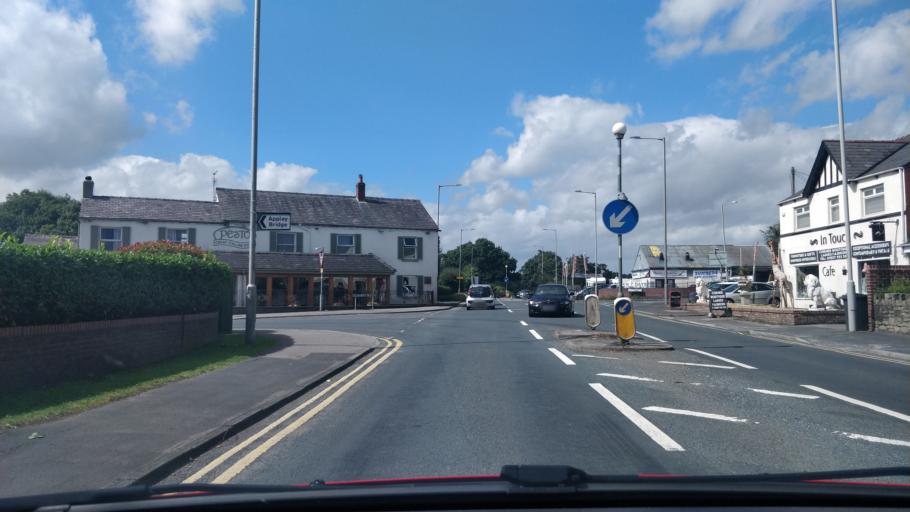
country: GB
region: England
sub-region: Lancashire
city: Appley Bridge
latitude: 53.5919
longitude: -2.7242
